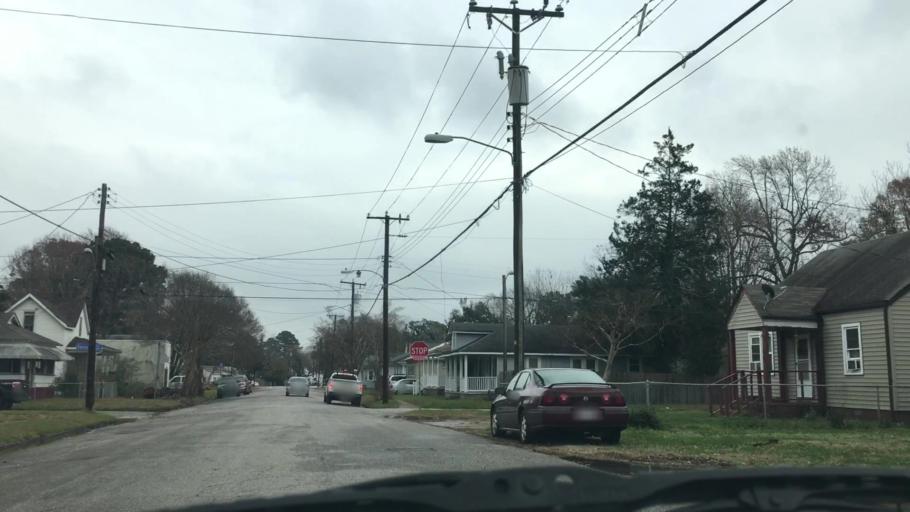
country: US
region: Virginia
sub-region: City of Norfolk
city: Norfolk
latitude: 36.8753
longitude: -76.2489
